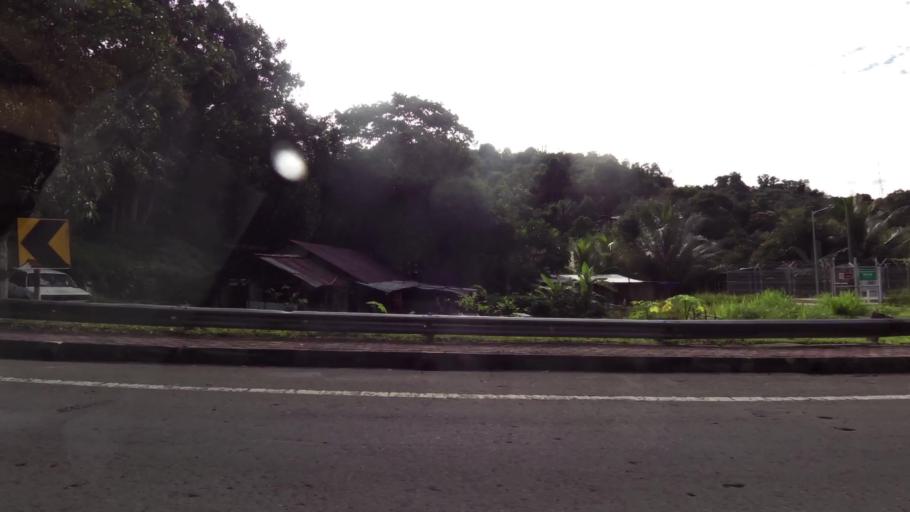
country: BN
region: Brunei and Muara
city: Bandar Seri Begawan
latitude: 4.8913
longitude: 114.9509
